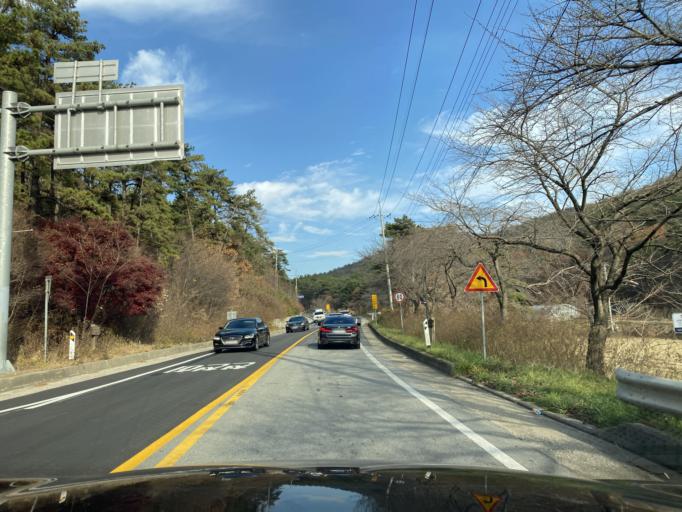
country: KR
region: Chungcheongnam-do
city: Hongsung
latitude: 36.6572
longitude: 126.6255
